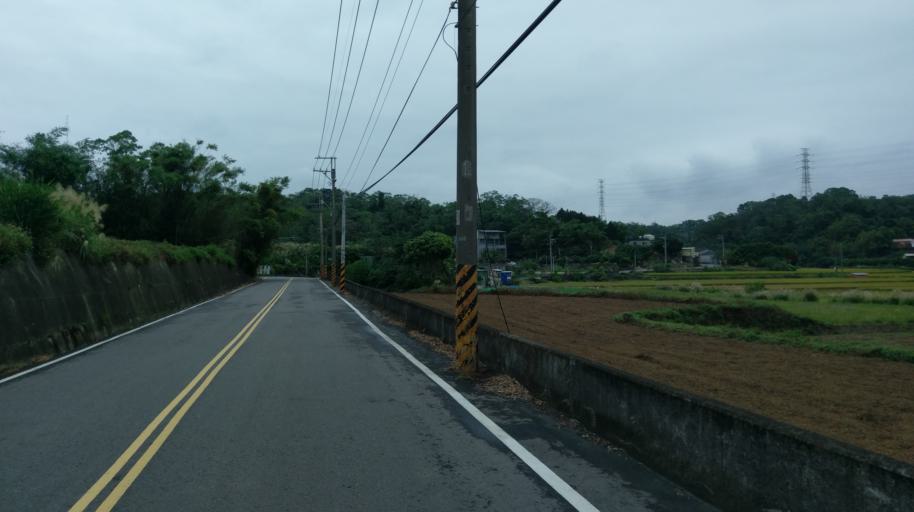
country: TW
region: Taiwan
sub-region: Hsinchu
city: Hsinchu
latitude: 24.7384
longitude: 120.9497
